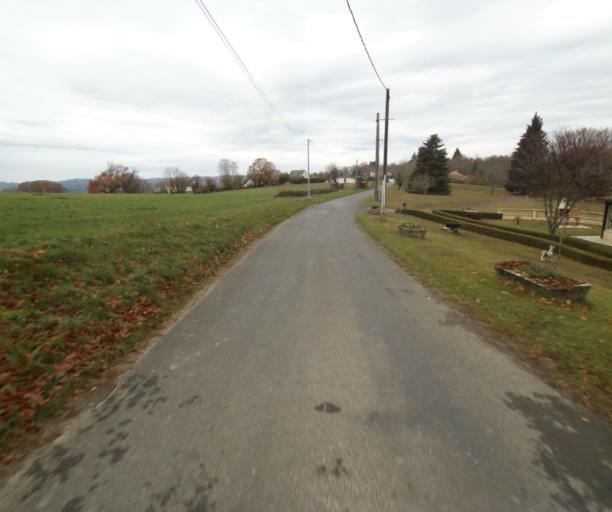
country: FR
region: Limousin
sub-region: Departement de la Correze
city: Sainte-Fortunade
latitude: 45.2286
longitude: 1.7633
